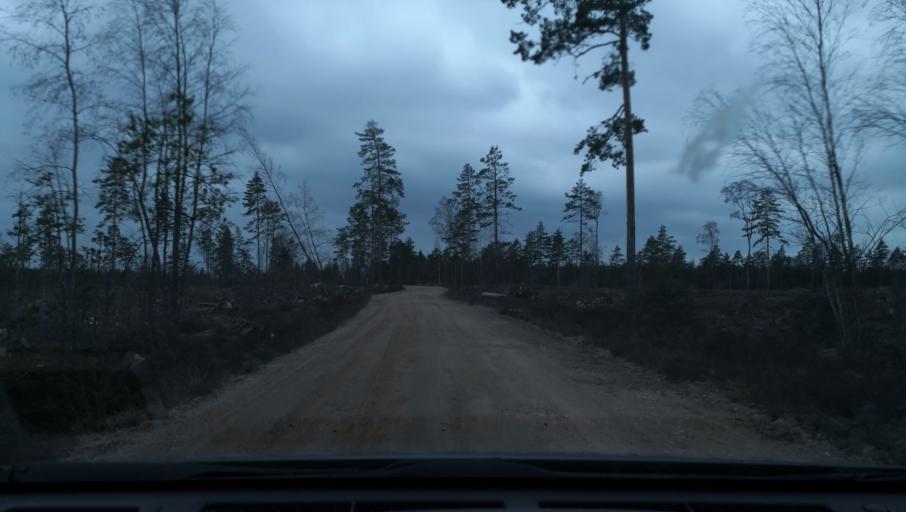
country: SE
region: OErebro
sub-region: Lindesbergs Kommun
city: Fellingsbro
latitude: 59.5955
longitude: 15.5785
